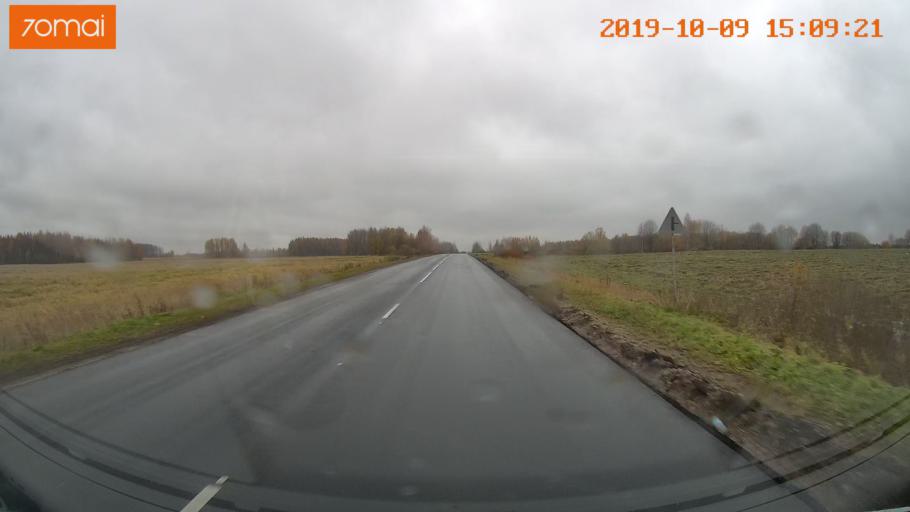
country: RU
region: Kostroma
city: Susanino
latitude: 58.1927
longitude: 41.6506
